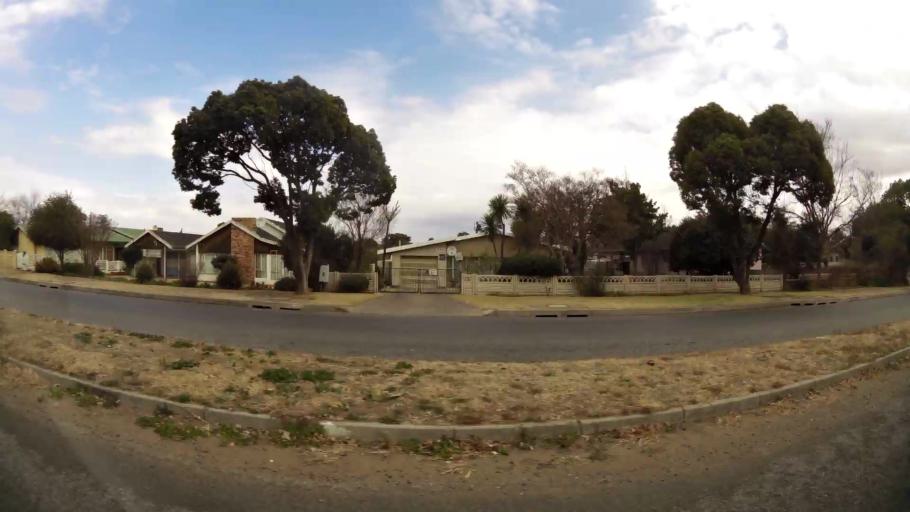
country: ZA
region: Orange Free State
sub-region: Fezile Dabi District Municipality
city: Kroonstad
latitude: -27.6424
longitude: 27.2270
